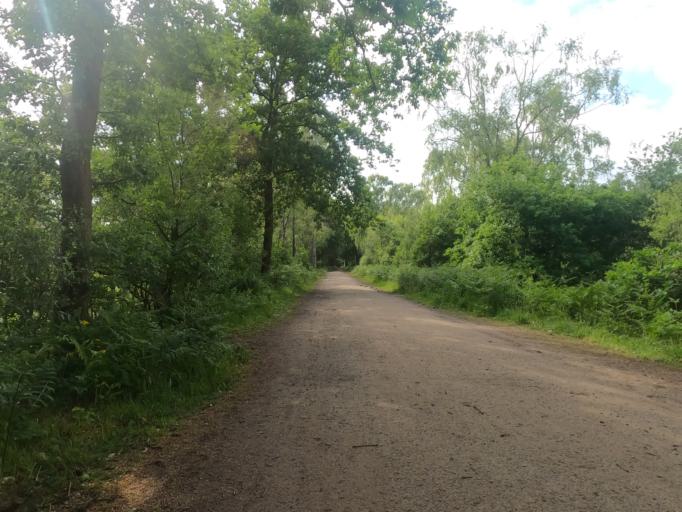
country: GB
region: England
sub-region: Cheshire West and Chester
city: Cuddington
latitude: 53.2140
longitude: -2.5978
